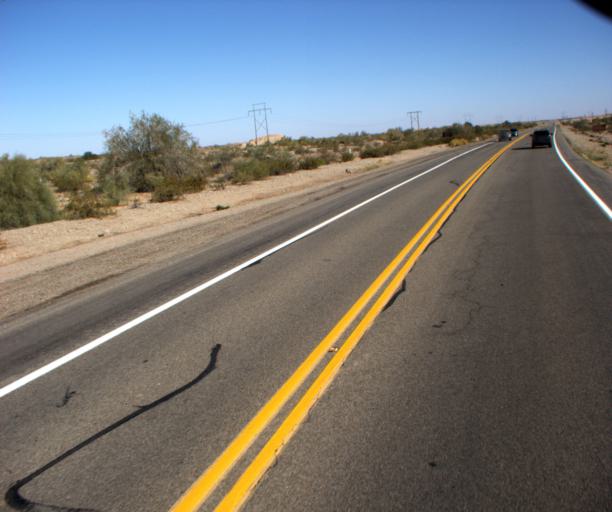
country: US
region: Arizona
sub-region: Yuma County
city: Fortuna Foothills
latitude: 32.7931
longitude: -114.3814
